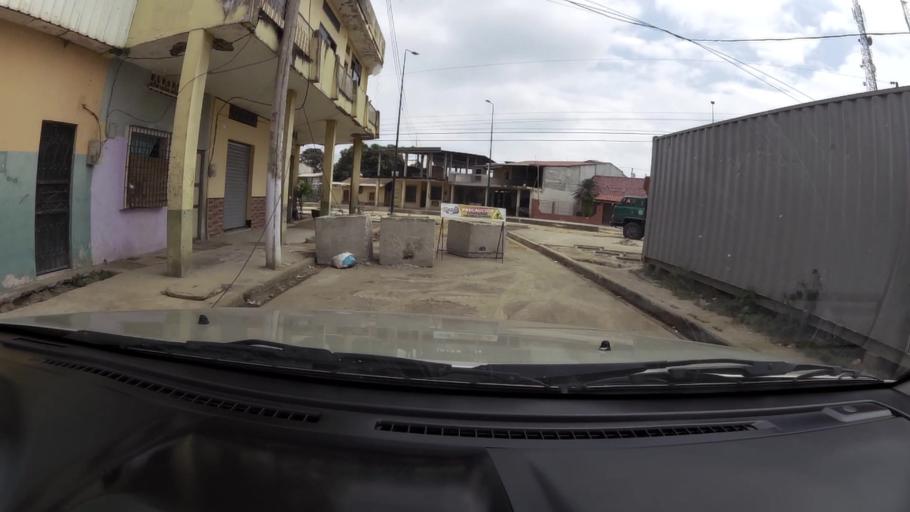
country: EC
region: El Oro
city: Pasaje
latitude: -3.2474
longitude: -79.8312
